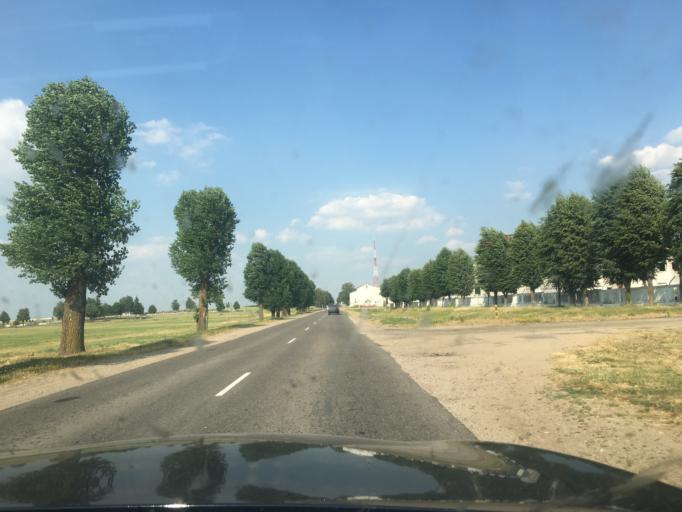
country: BY
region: Grodnenskaya
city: Svislach
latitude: 53.0406
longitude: 24.0804
